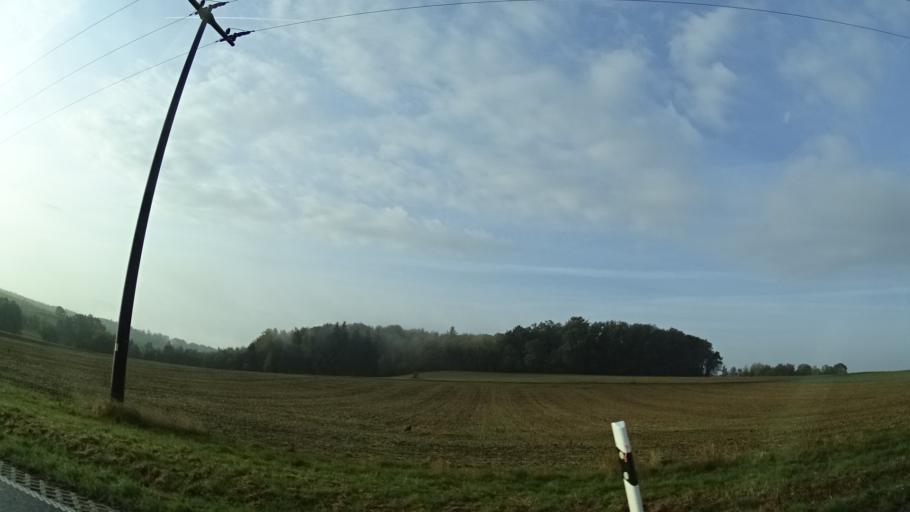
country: DE
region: Hesse
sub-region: Regierungsbezirk Darmstadt
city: Hirzenhain
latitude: 50.4142
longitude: 9.1392
